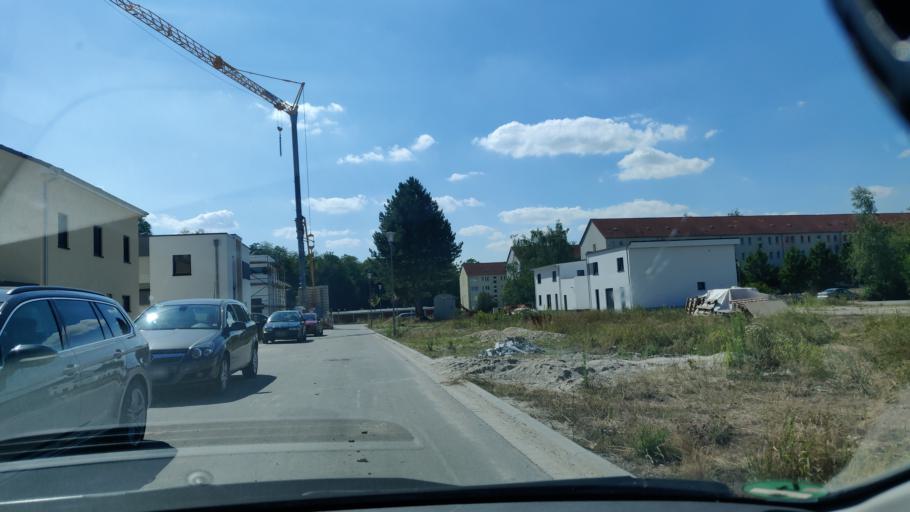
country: DE
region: Saxony
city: Borna
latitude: 51.1327
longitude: 12.4916
